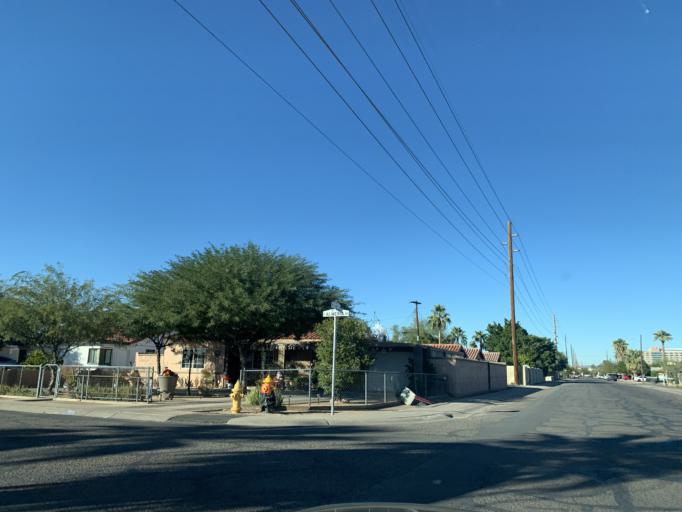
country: US
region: Arizona
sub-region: Maricopa County
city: Phoenix
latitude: 33.4666
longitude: -112.0434
